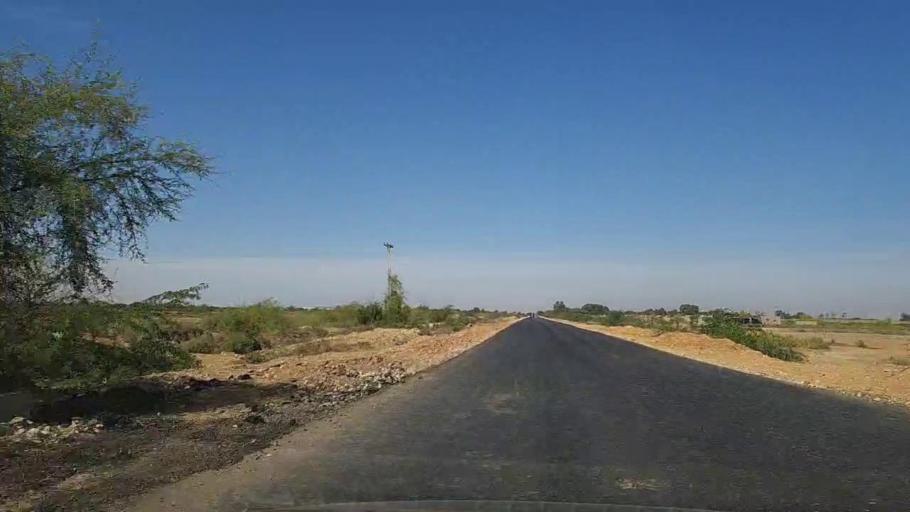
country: PK
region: Sindh
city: Kotri
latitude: 25.2243
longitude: 68.2370
